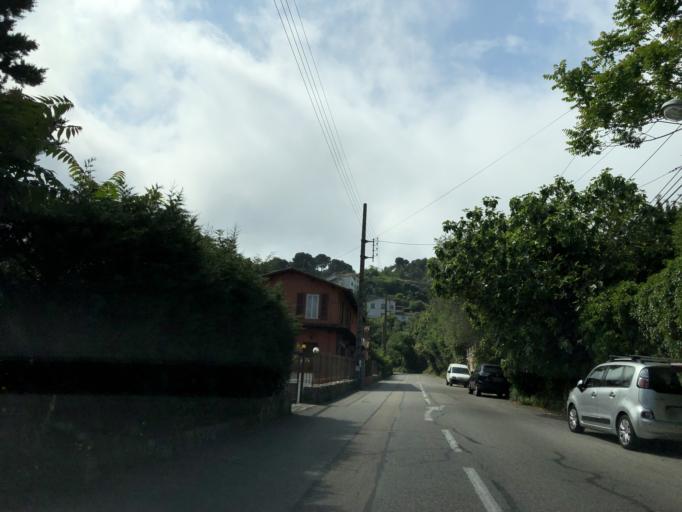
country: FR
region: Provence-Alpes-Cote d'Azur
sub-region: Departement des Alpes-Maritimes
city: Villefranche-sur-Mer
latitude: 43.7183
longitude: 7.3102
